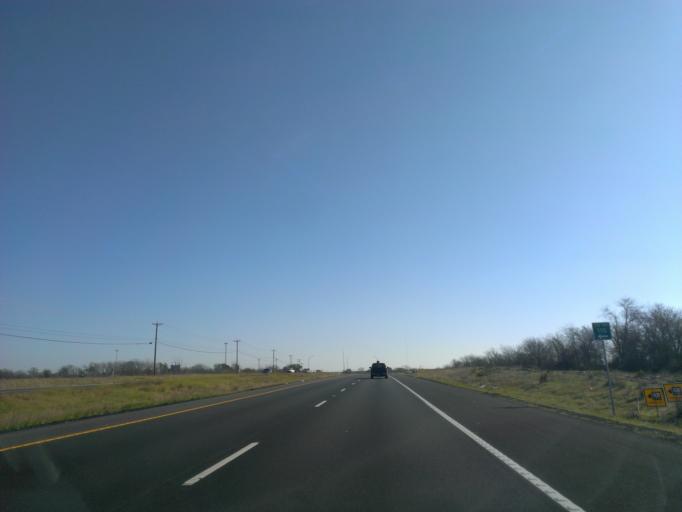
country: US
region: Texas
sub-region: Williamson County
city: Hutto
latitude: 30.5331
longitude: -97.6052
